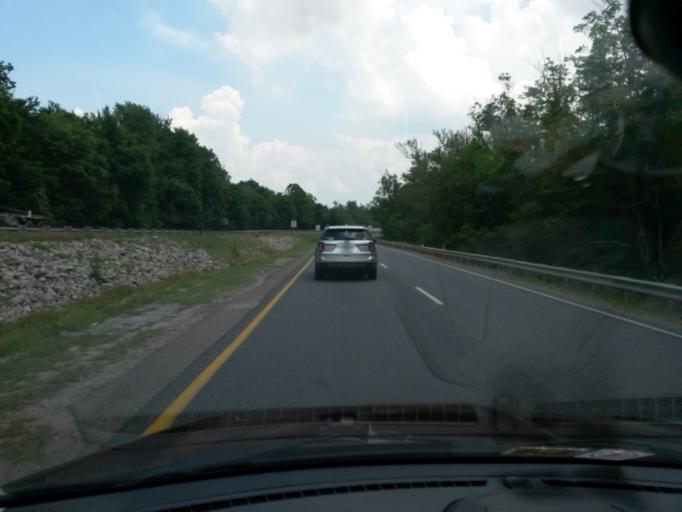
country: US
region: Virginia
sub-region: City of Hopewell
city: Hopewell
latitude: 37.3168
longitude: -77.3009
